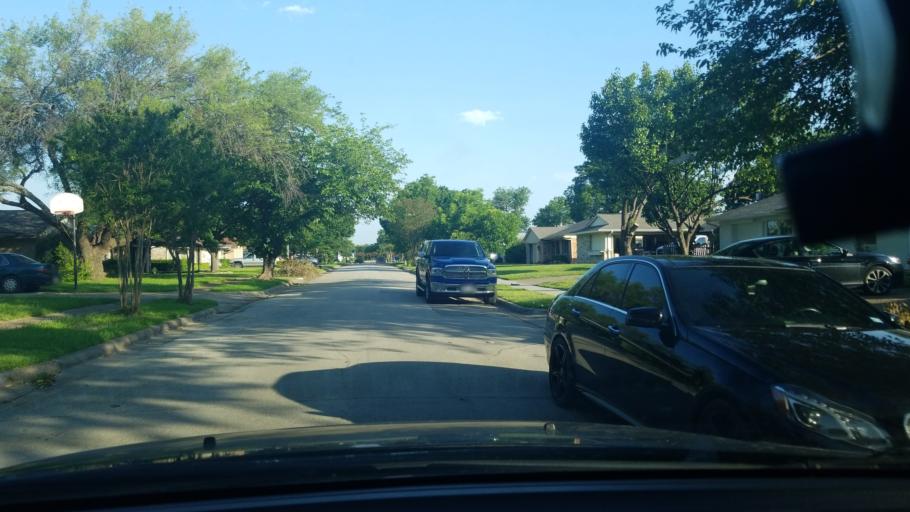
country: US
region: Texas
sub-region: Dallas County
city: Mesquite
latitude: 32.8021
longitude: -96.6417
